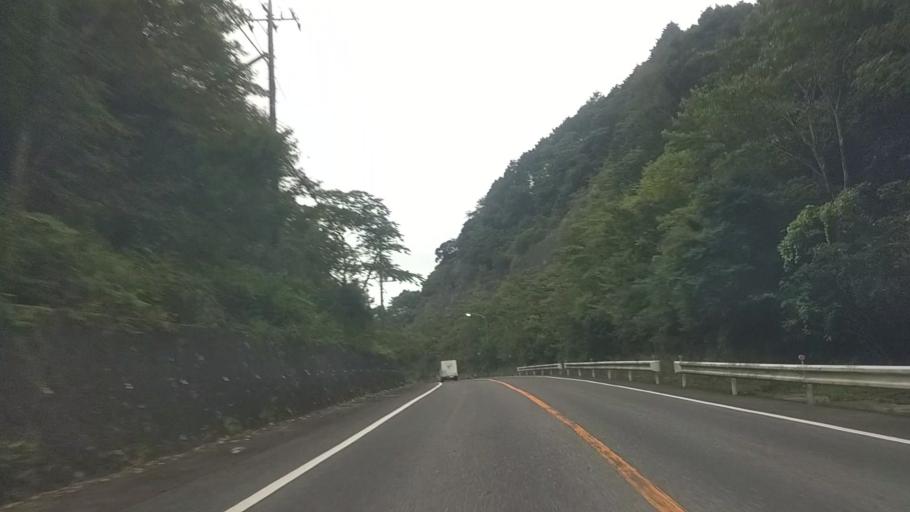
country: JP
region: Chiba
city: Kawaguchi
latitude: 35.1674
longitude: 140.0601
